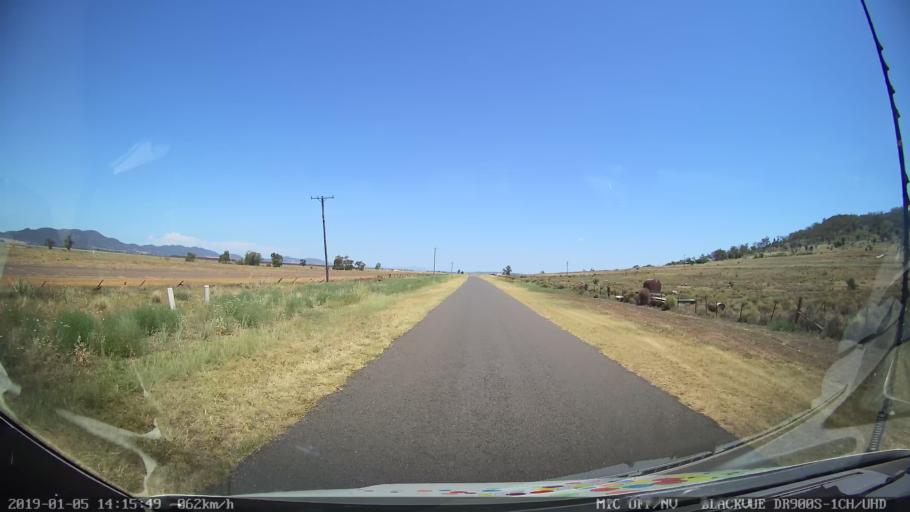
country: AU
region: New South Wales
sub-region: Liverpool Plains
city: Quirindi
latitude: -31.2505
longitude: 150.4715
